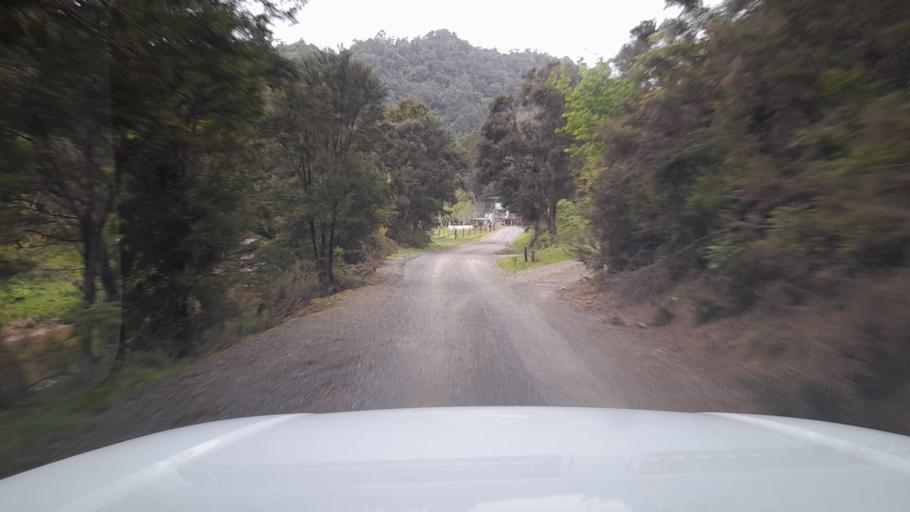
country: NZ
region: Northland
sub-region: Far North District
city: Paihia
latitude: -35.3539
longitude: 174.2341
